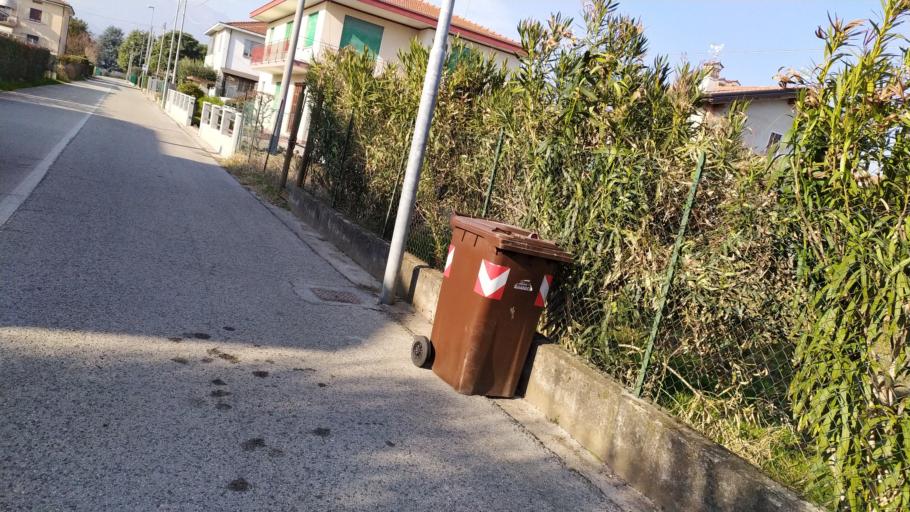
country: IT
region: Veneto
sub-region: Provincia di Vicenza
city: Giavenale
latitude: 45.6901
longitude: 11.3993
